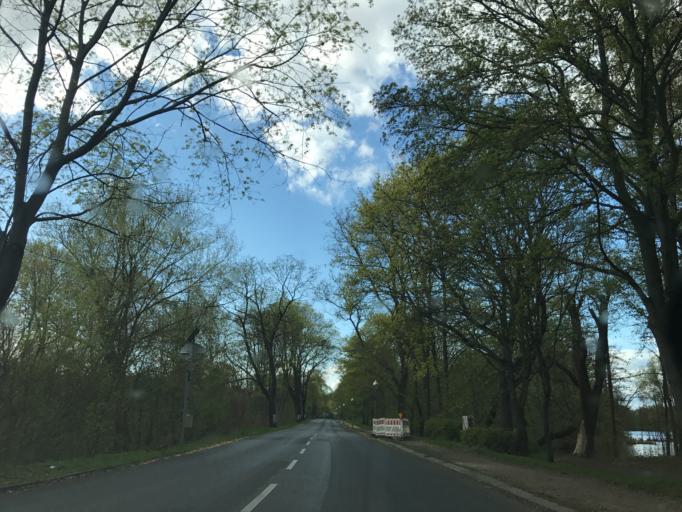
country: DE
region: Berlin
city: Haselhorst
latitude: 52.5504
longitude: 13.2360
